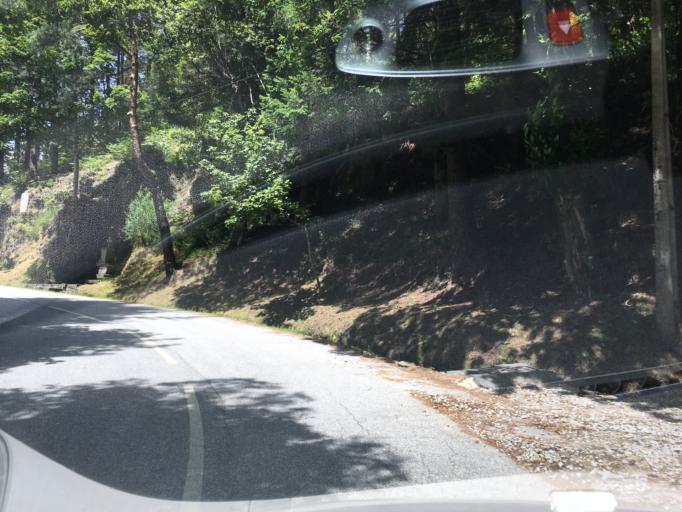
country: PT
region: Vila Real
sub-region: Mesao Frio
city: Mesao Frio
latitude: 41.2768
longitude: -7.9249
